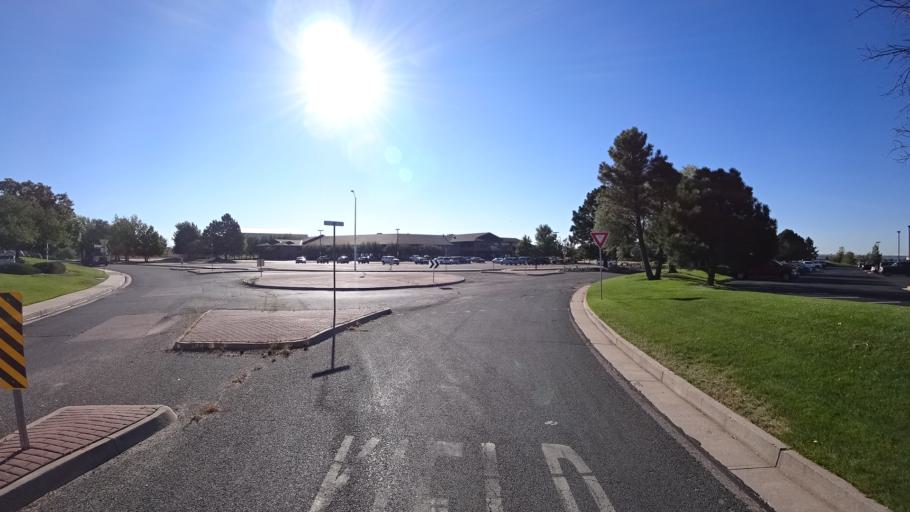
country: US
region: Colorado
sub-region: El Paso County
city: Cimarron Hills
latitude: 38.8079
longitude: -104.7270
